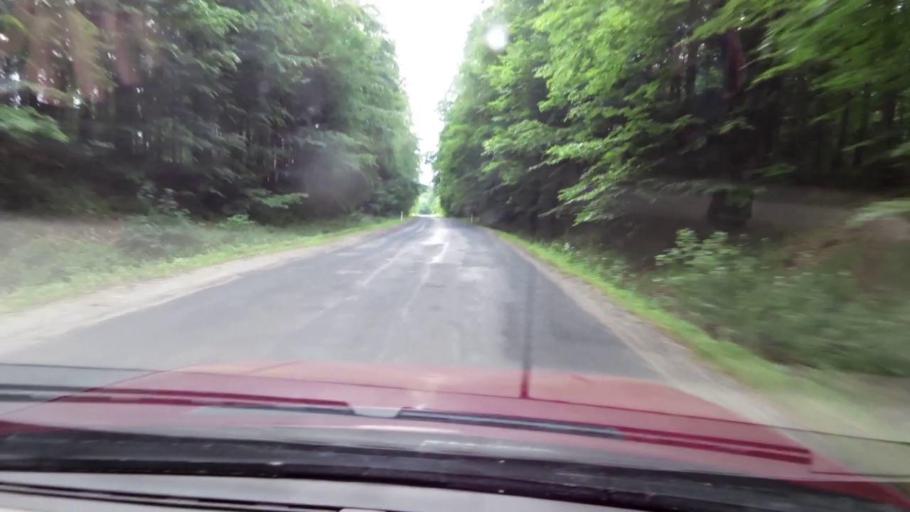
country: PL
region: Pomeranian Voivodeship
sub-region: Powiat slupski
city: Kepice
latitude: 54.2705
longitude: 16.9925
